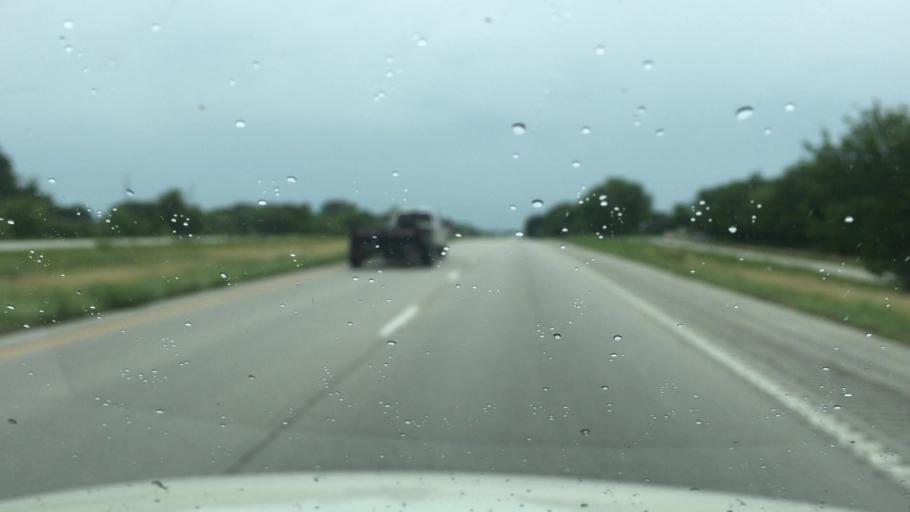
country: US
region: Missouri
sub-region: Jackson County
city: Lake Lotawana
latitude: 38.8854
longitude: -94.2308
